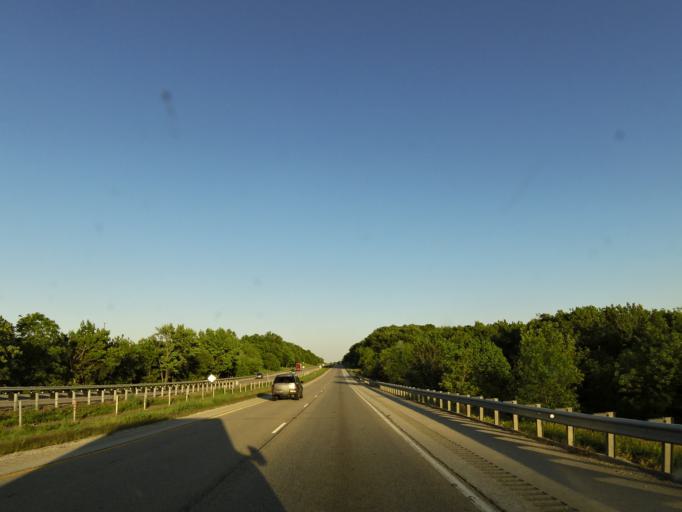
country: US
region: Illinois
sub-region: Vermilion County
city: Tilton
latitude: 40.1144
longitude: -87.6926
